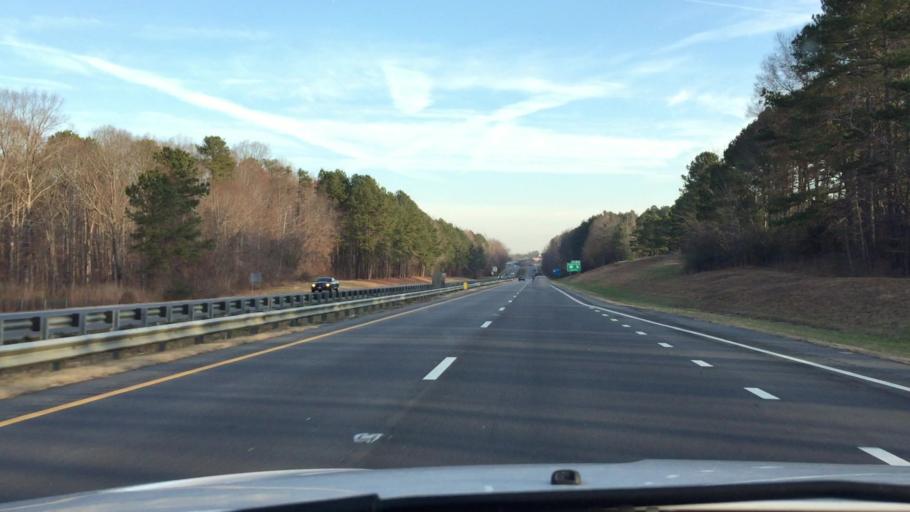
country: US
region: North Carolina
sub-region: Lee County
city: Sanford
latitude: 35.4729
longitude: -79.2015
